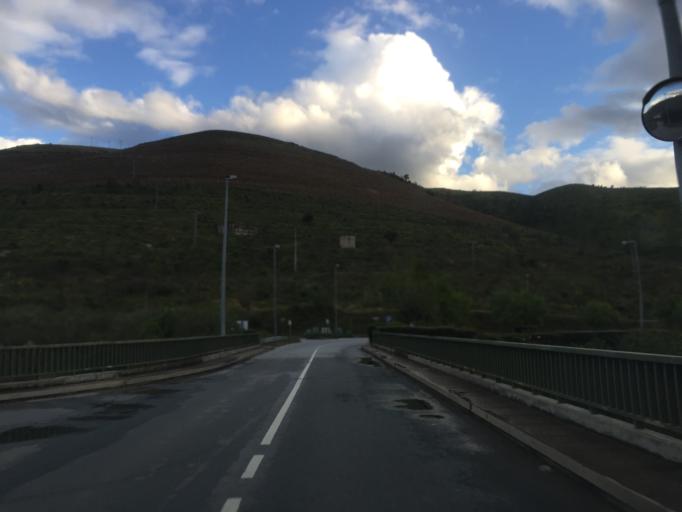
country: PT
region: Braganca
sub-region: Torre de Moncorvo
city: Torre de Moncorvo
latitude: 41.1331
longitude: -7.1137
